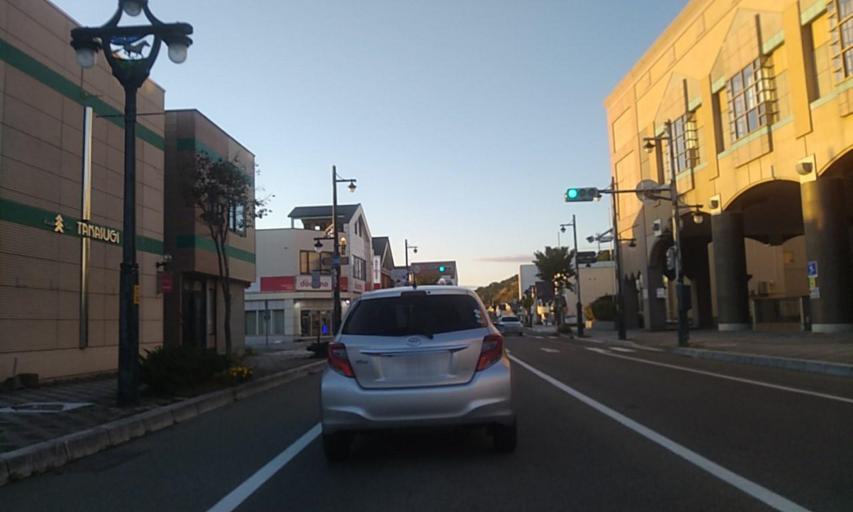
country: JP
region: Hokkaido
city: Shizunai-furukawacho
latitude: 42.1621
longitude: 142.7750
